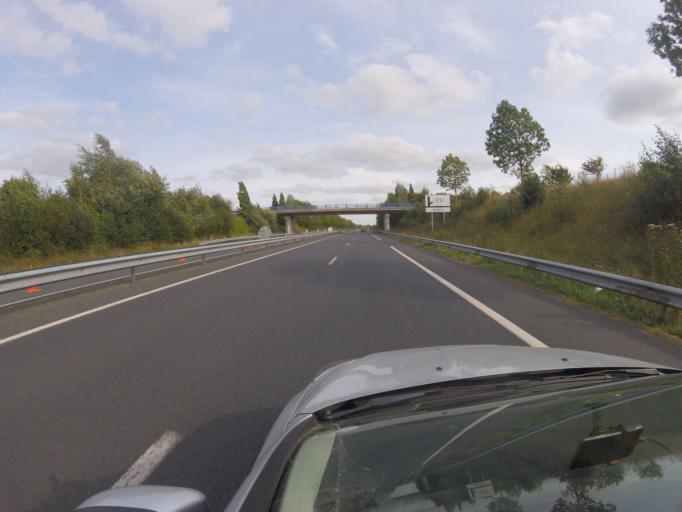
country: FR
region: Lower Normandy
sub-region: Departement de la Manche
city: Pont-Hebert
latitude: 49.1188
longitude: -1.1683
